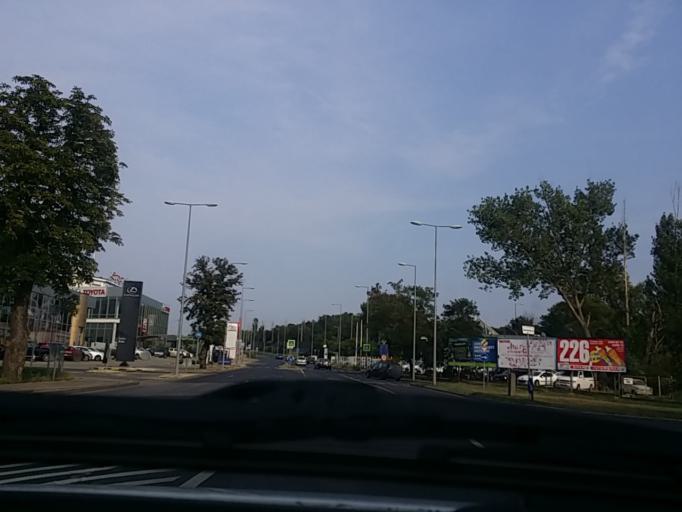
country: HU
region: Budapest
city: Budapest XII. keruelet
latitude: 47.4615
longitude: 18.9977
